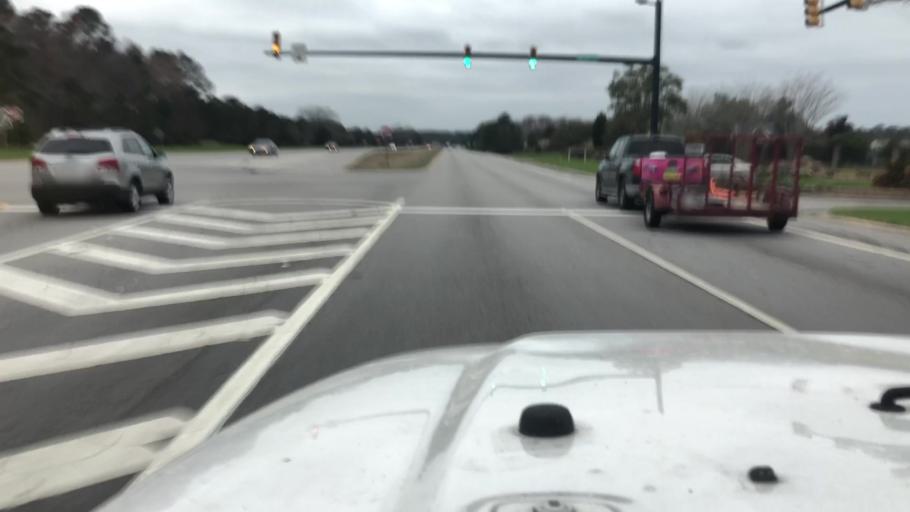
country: US
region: South Carolina
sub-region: Beaufort County
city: Bluffton
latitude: 32.3008
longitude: -80.9557
